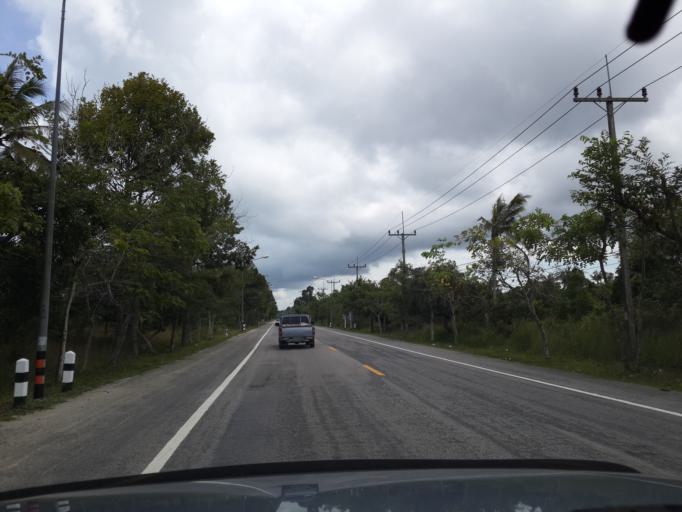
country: TH
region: Narathiwat
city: Narathiwat
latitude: 6.4962
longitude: 101.7708
